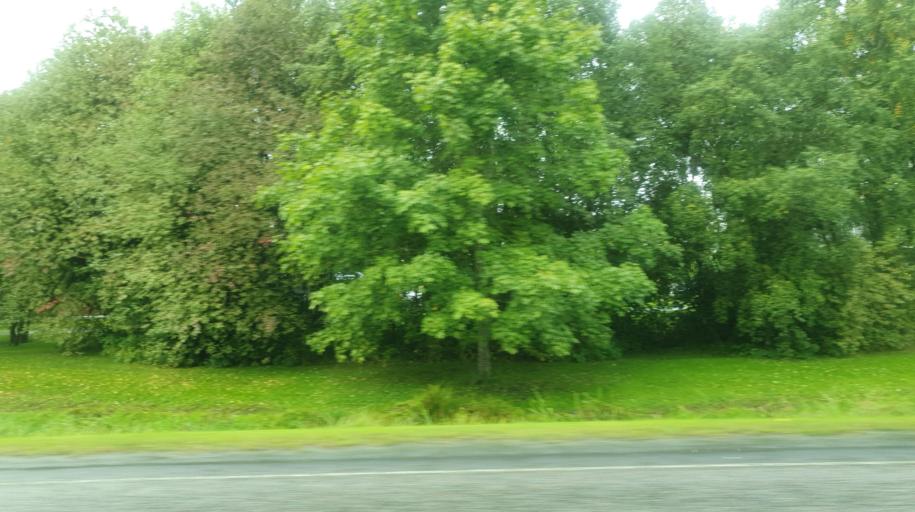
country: NO
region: Nord-Trondelag
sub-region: Verdal
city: Verdal
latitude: 63.7902
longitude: 11.4884
